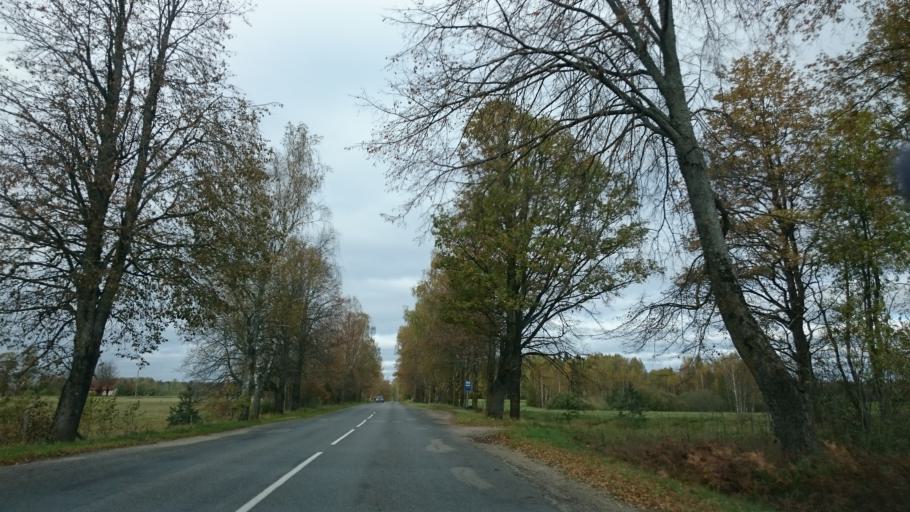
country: LV
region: Amatas Novads
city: Drabesi
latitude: 57.2706
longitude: 25.2732
